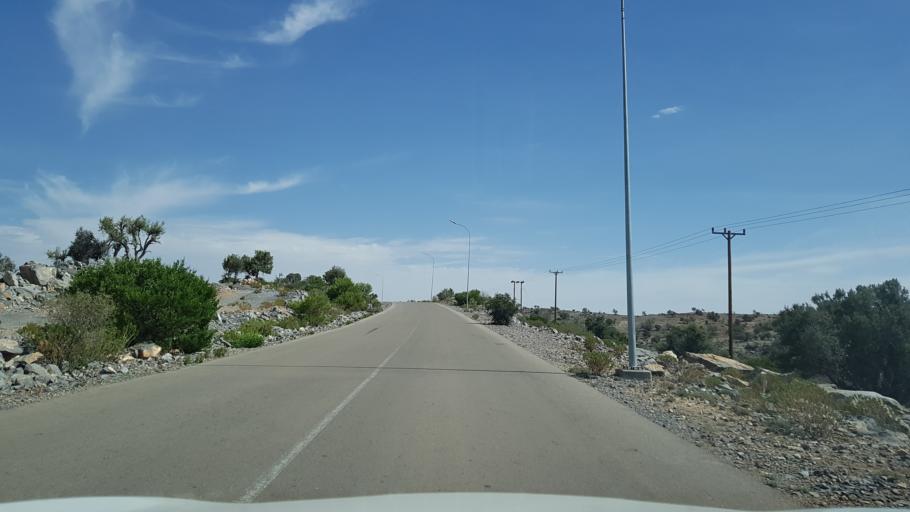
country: OM
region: Al Batinah
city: Bayt al `Awabi
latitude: 23.1270
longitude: 57.5991
